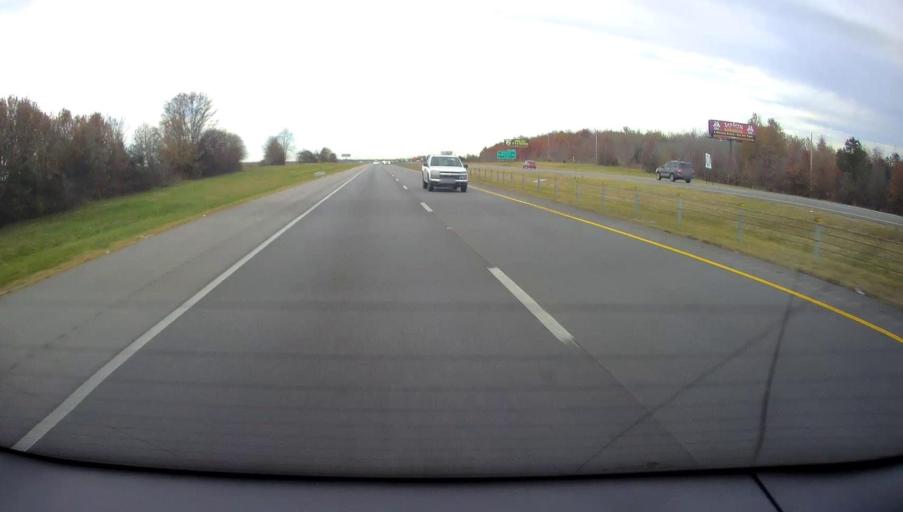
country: US
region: Alabama
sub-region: Limestone County
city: Athens
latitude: 34.7167
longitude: -86.9318
